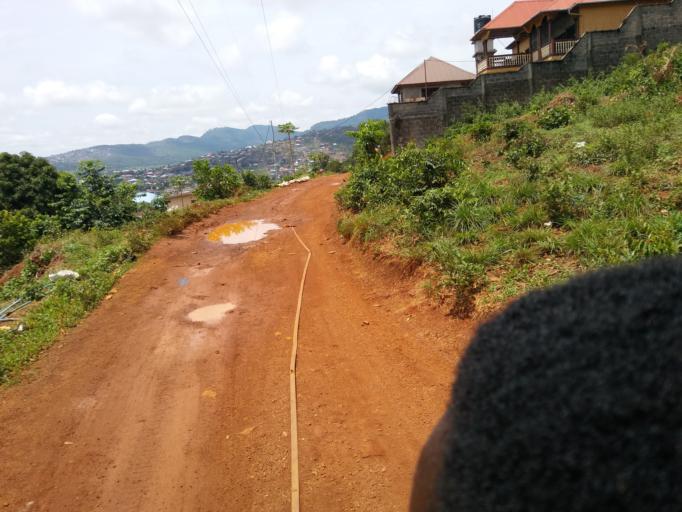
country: SL
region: Western Area
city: Hastings
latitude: 8.3891
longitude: -13.1601
